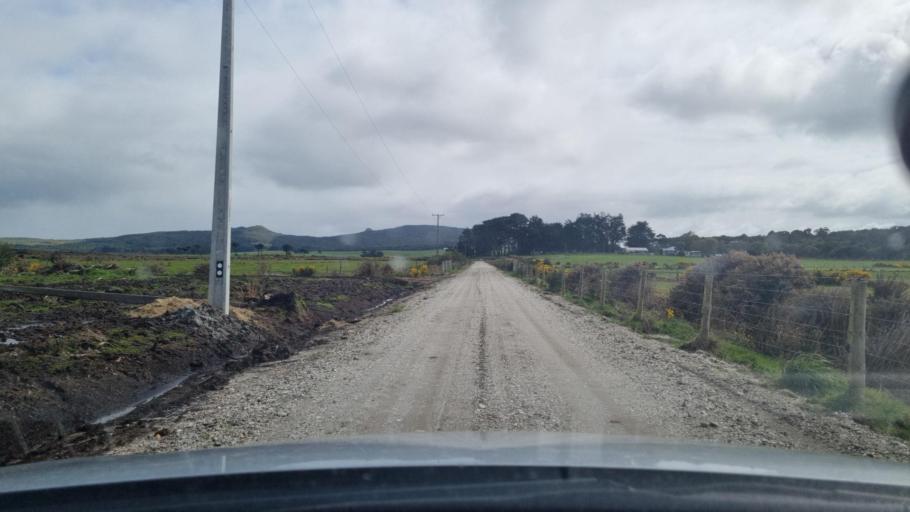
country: NZ
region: Southland
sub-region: Invercargill City
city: Bluff
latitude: -46.5258
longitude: 168.3034
